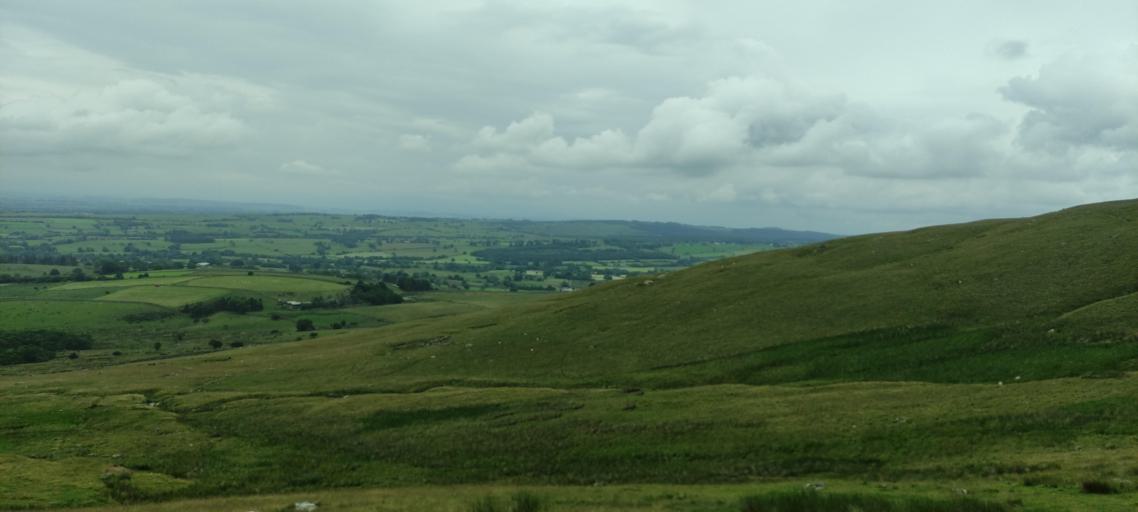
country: GB
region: England
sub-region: Cumbria
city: Keswick
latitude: 54.7132
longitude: -3.0325
